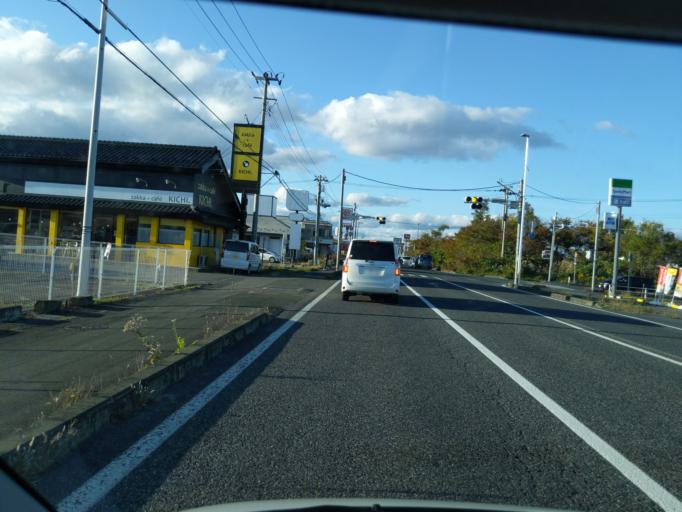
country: JP
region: Iwate
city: Kitakami
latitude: 39.2174
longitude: 141.1009
